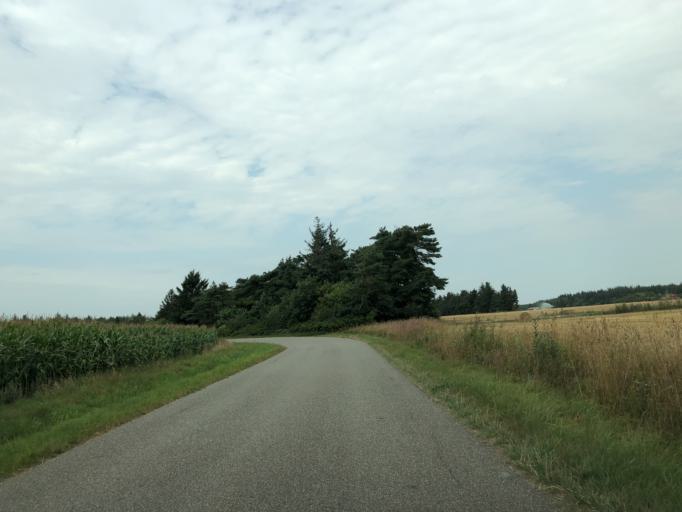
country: DK
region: Central Jutland
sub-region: Holstebro Kommune
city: Ulfborg
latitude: 56.1824
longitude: 8.3209
